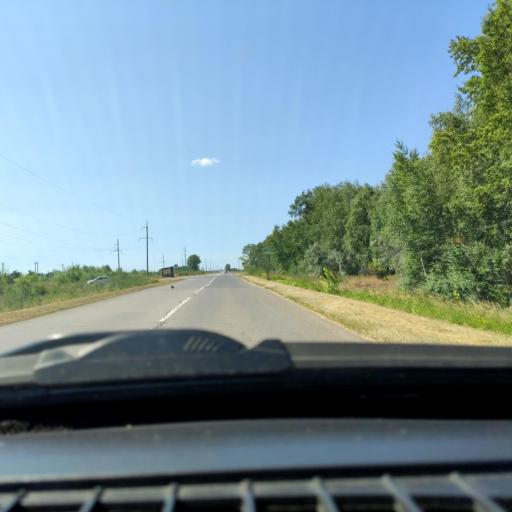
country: RU
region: Samara
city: Tol'yatti
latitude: 53.7308
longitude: 49.4110
